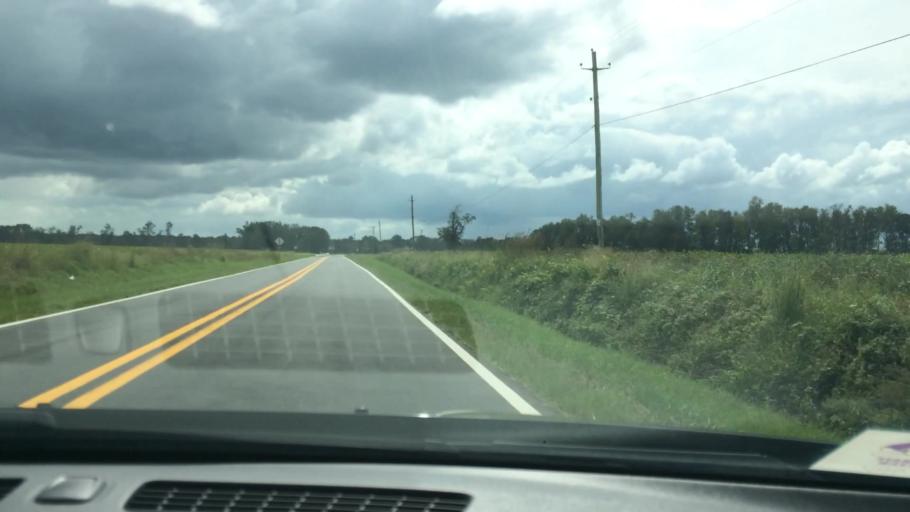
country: US
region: North Carolina
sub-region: Pitt County
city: Farmville
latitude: 35.5477
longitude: -77.5450
